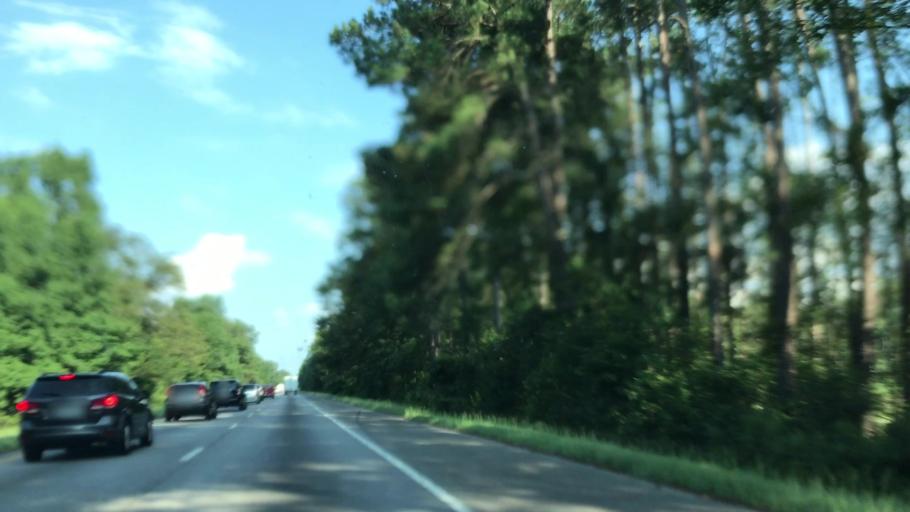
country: US
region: South Carolina
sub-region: Dorchester County
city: Saint George
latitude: 33.3692
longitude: -80.6056
